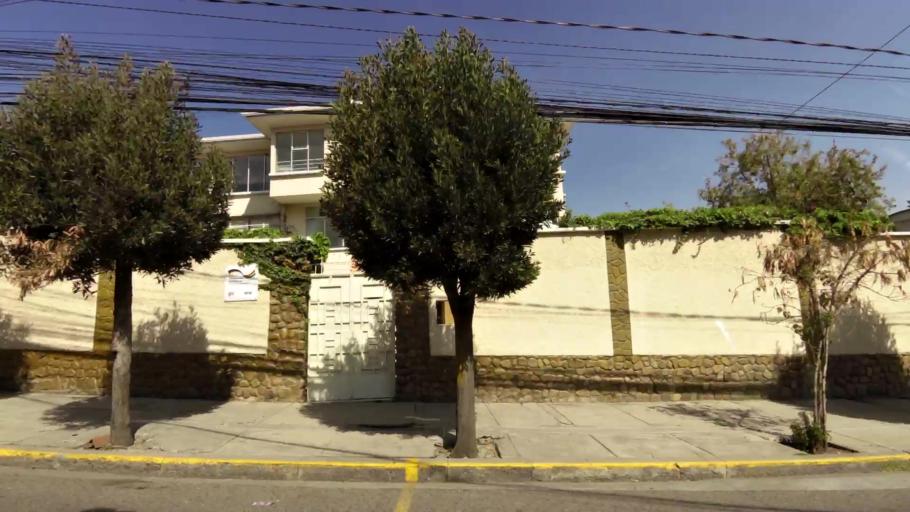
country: BO
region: La Paz
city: La Paz
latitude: -16.5407
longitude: -68.0813
